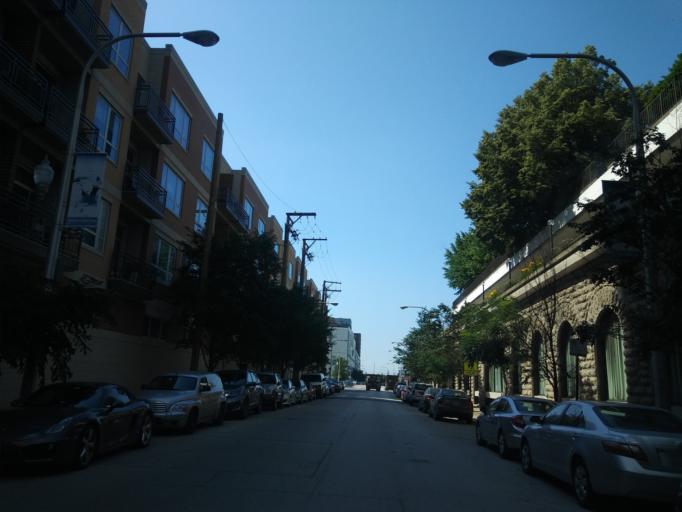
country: US
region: Illinois
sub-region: Cook County
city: Chicago
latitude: 41.8718
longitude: -87.6336
